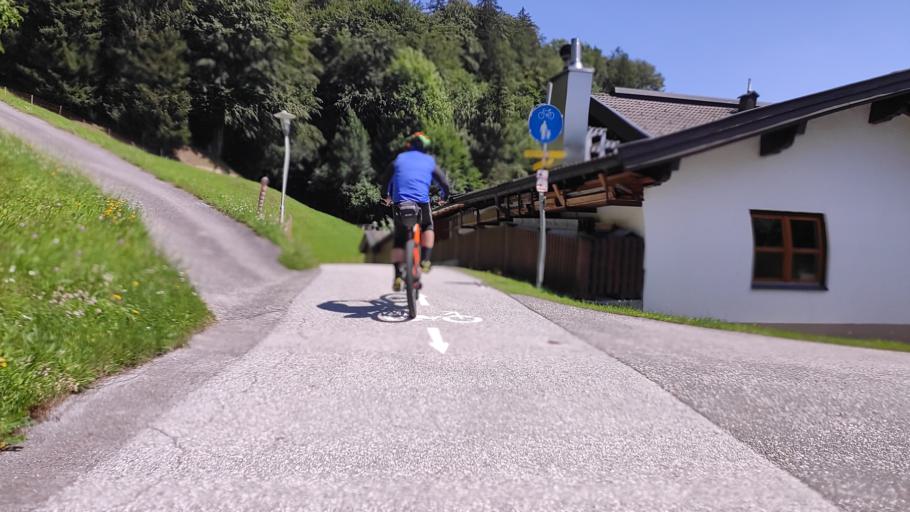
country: AT
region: Salzburg
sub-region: Politischer Bezirk Zell am See
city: Leogang
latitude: 47.4404
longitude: 12.7481
